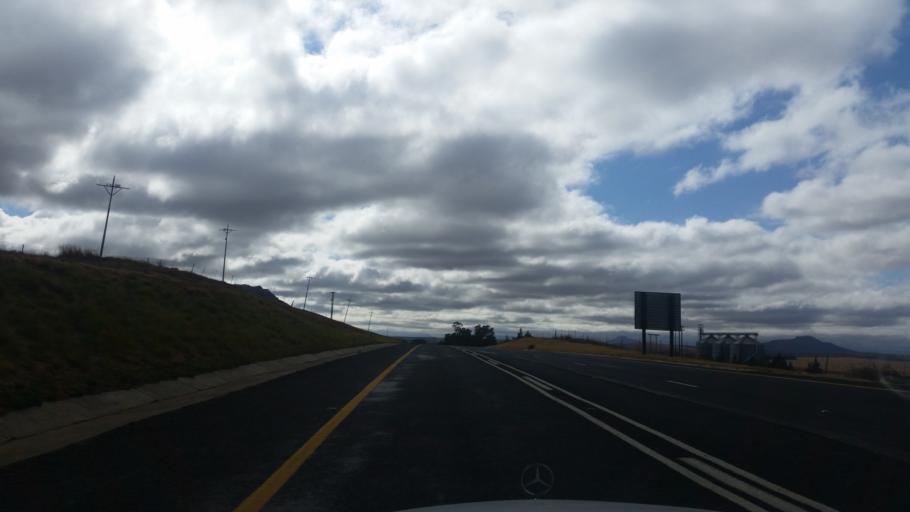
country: ZA
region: Orange Free State
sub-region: Thabo Mofutsanyana District Municipality
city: Phuthaditjhaba
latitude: -28.3134
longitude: 28.7219
